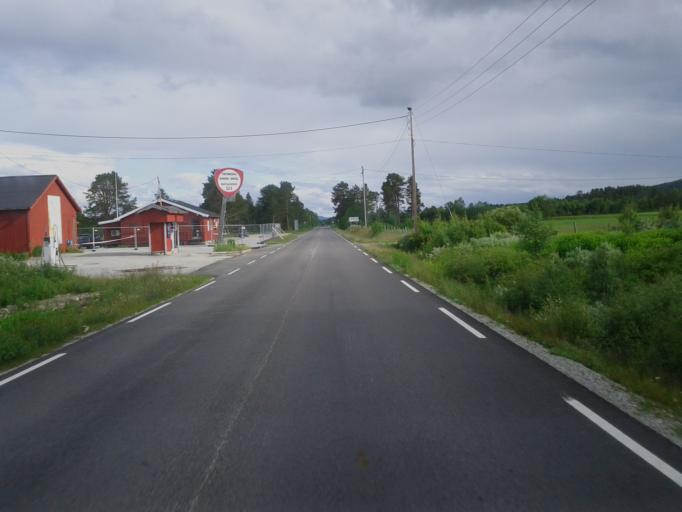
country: NO
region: Sor-Trondelag
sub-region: Roros
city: Roros
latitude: 62.2870
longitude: 11.7343
